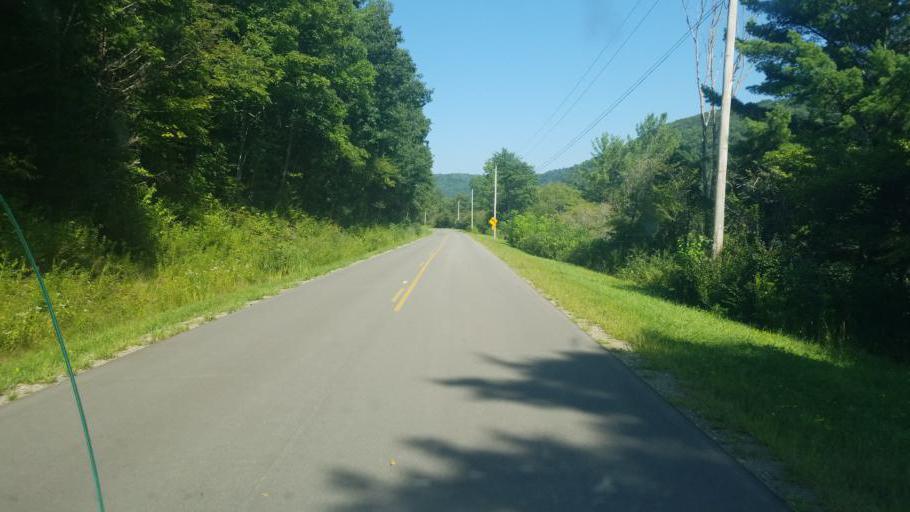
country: US
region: New York
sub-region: Allegany County
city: Wellsville
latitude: 42.0137
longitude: -78.0122
